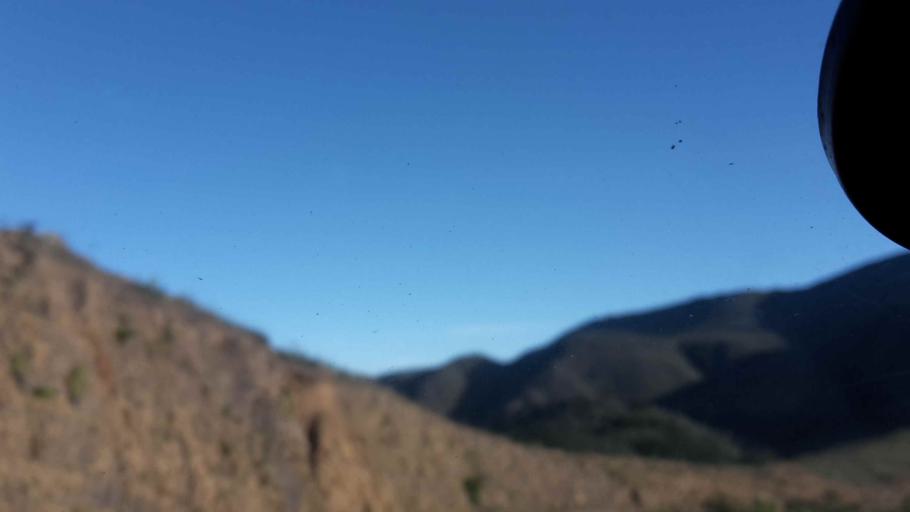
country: BO
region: Cochabamba
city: Arani
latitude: -17.7916
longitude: -65.5995
